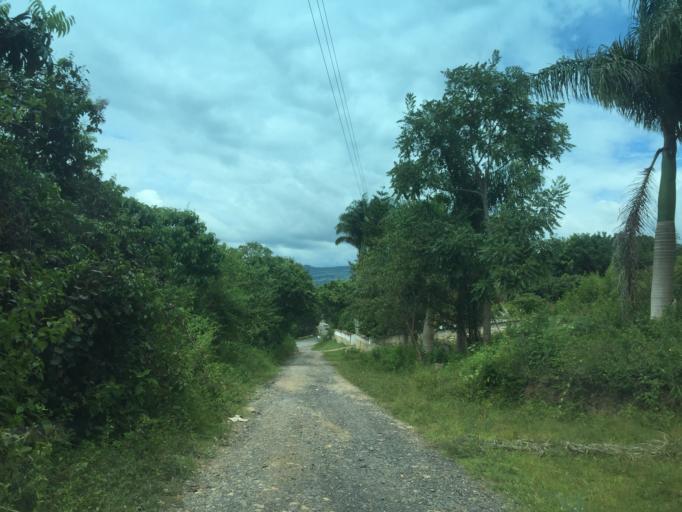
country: CO
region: Santander
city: Guepsa
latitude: 6.0229
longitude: -73.5497
